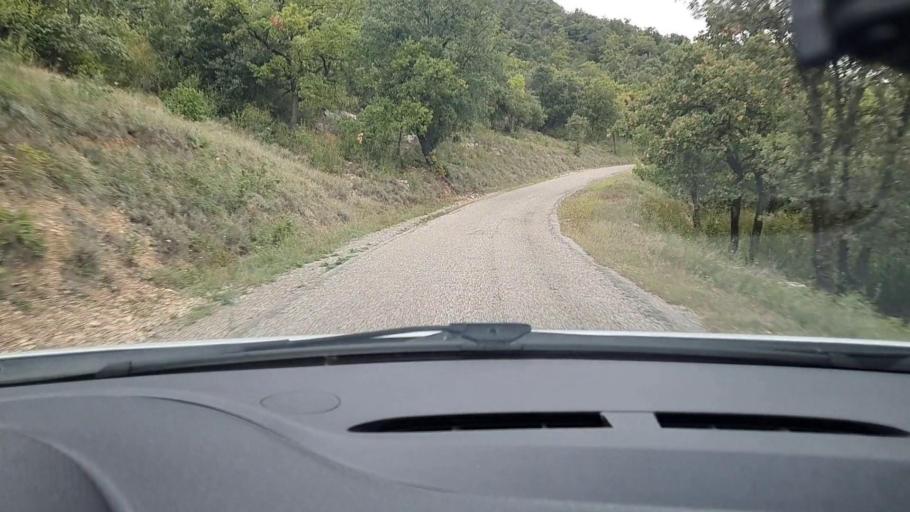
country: FR
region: Languedoc-Roussillon
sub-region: Departement du Gard
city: Mons
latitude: 44.1298
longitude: 4.2889
